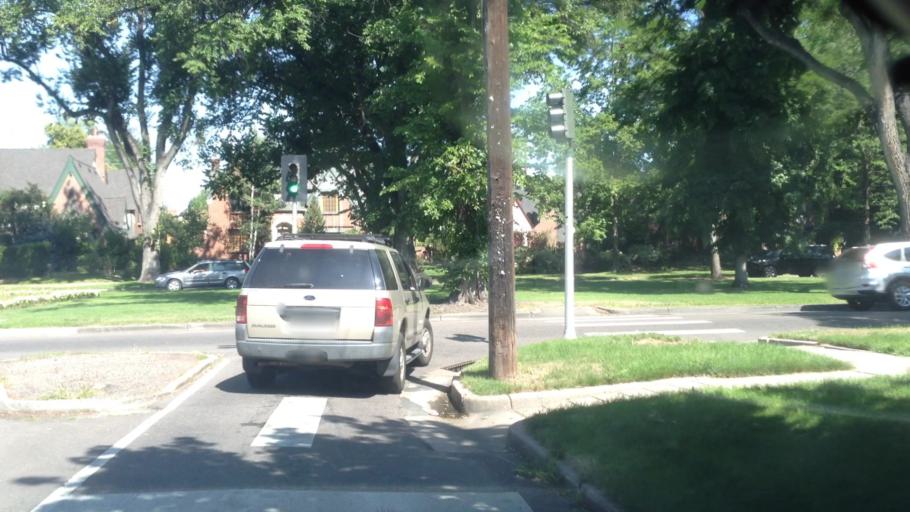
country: US
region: Colorado
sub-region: Arapahoe County
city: Glendale
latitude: 39.7434
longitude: -104.9130
